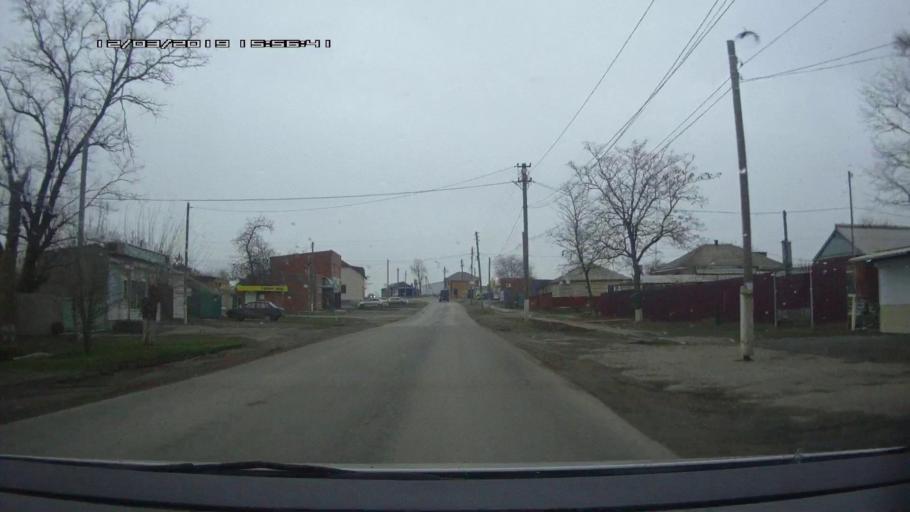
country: RU
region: Rostov
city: Novobataysk
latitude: 46.9016
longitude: 39.7817
